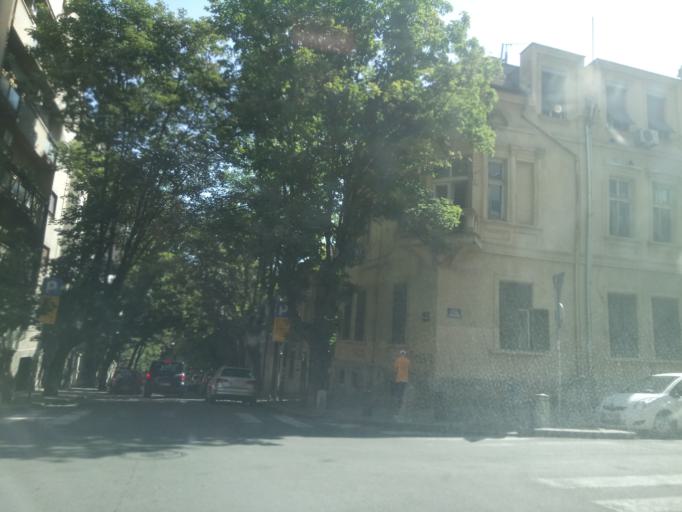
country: RS
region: Central Serbia
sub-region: Belgrade
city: Stari Grad
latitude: 44.8233
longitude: 20.4565
